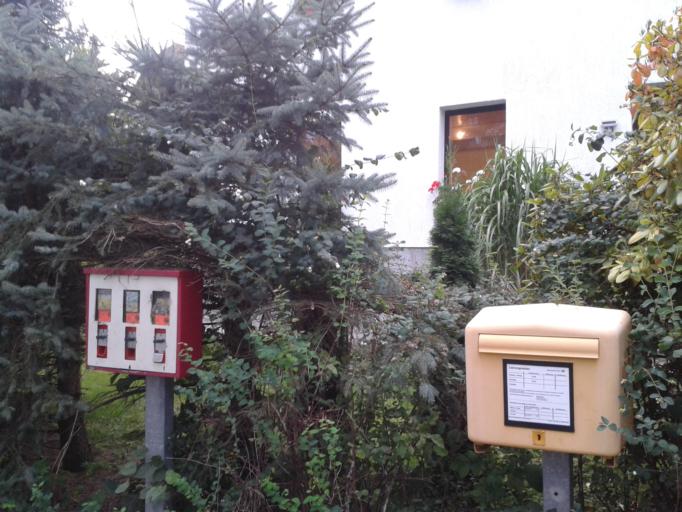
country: DE
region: Saxony
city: Freiberg
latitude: 50.9292
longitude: 13.3371
